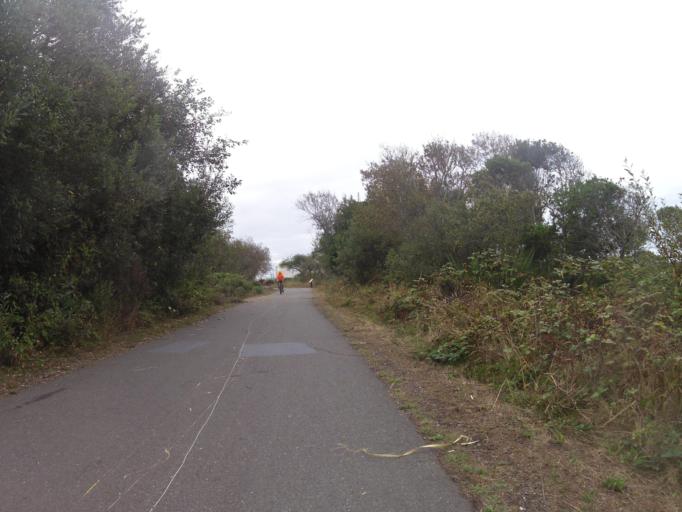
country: US
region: California
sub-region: Humboldt County
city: Bayview
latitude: 40.7798
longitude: -124.1930
